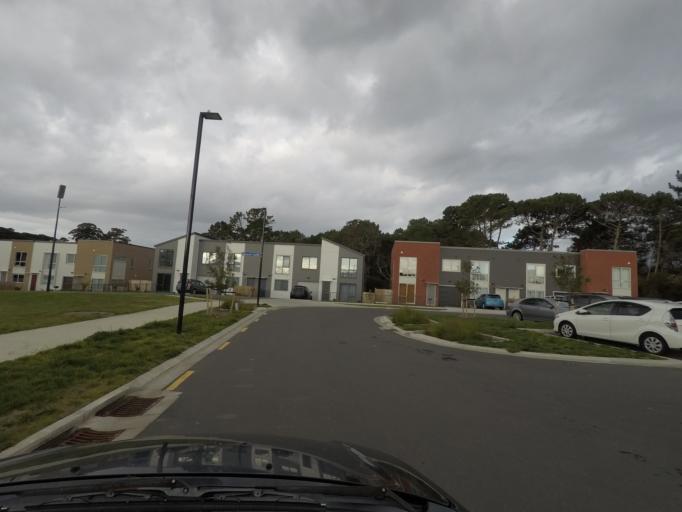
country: NZ
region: Auckland
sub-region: Auckland
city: Rosebank
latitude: -36.8262
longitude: 174.6277
